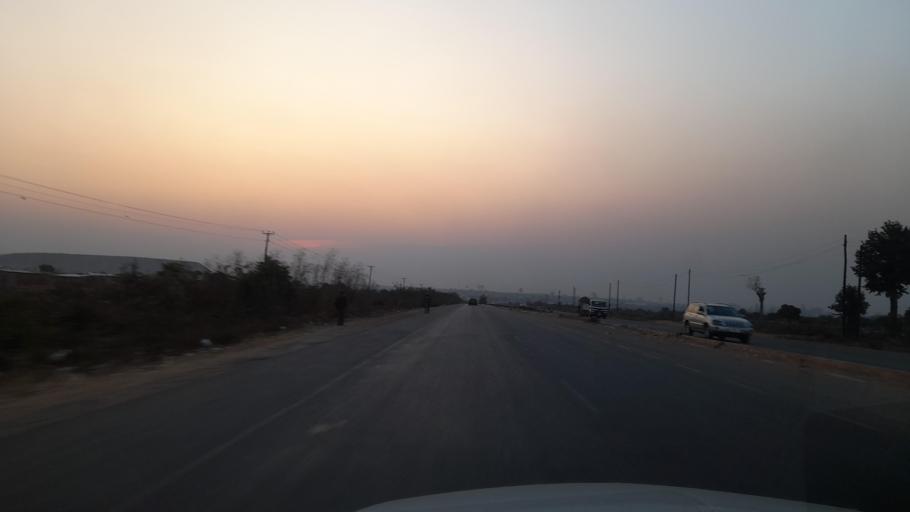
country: ZM
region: Copperbelt
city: Kitwe
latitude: -12.7680
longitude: 28.1785
